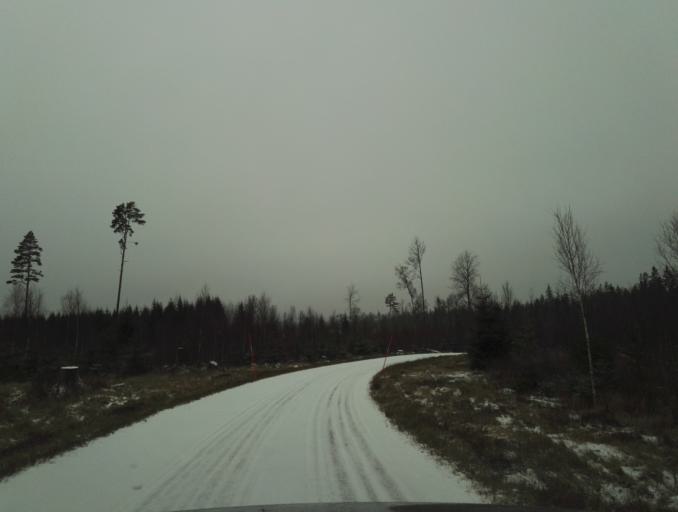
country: SE
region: Kronoberg
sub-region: Alvesta Kommun
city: Vislanda
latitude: 56.6886
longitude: 14.4246
